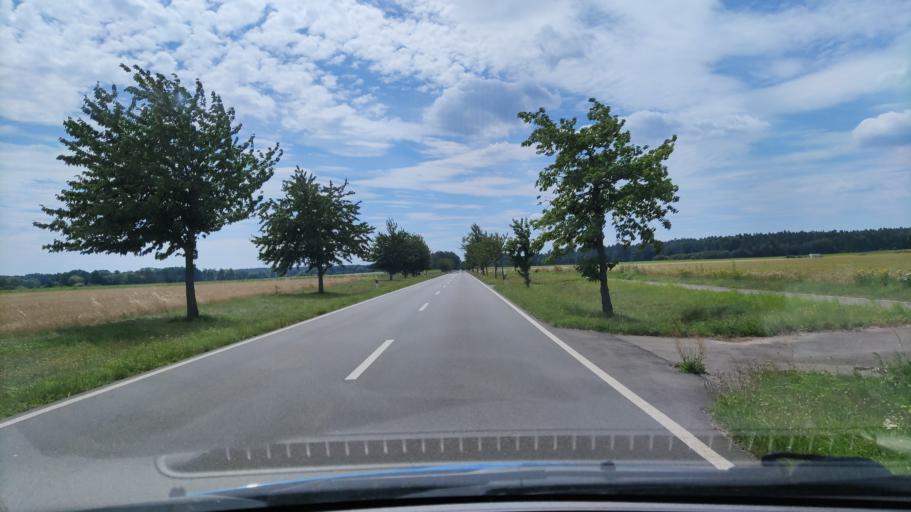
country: DE
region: Lower Saxony
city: Clenze
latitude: 52.9243
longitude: 10.9490
